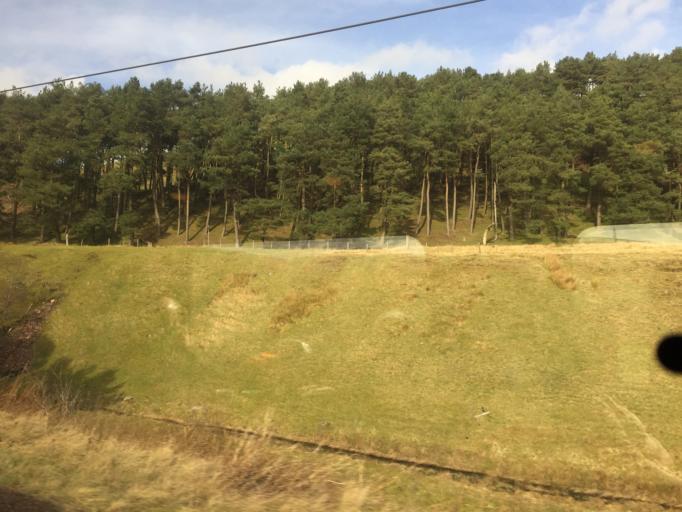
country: GB
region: Scotland
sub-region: South Lanarkshire
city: Douglas
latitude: 55.4731
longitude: -3.6804
